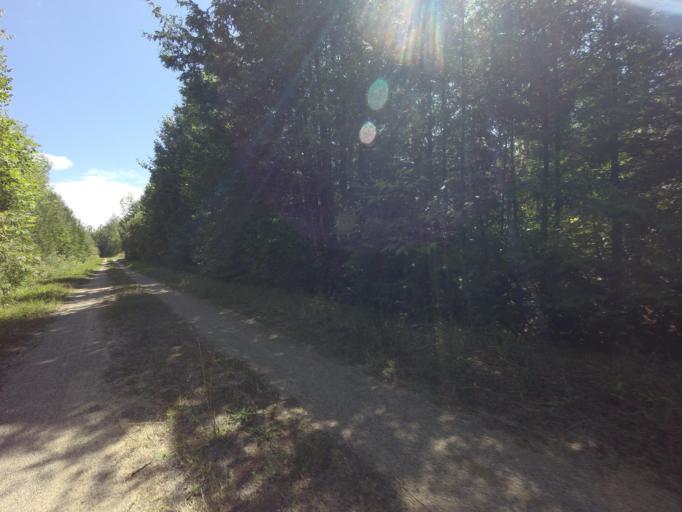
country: CA
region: Ontario
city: Orangeville
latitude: 43.7740
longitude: -80.1936
